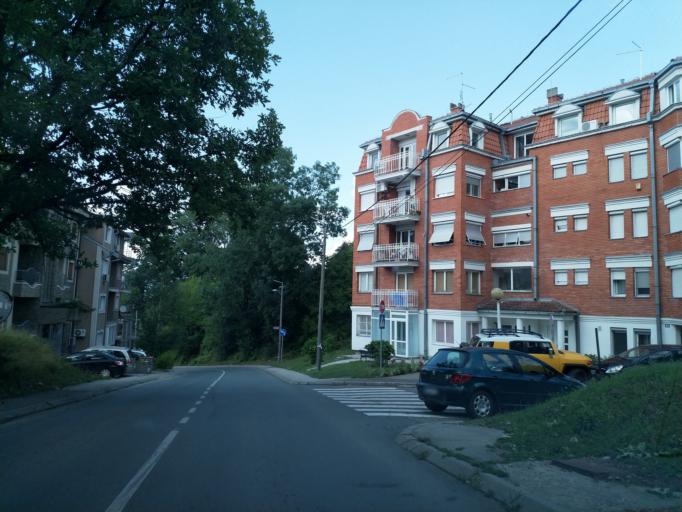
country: RS
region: Central Serbia
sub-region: Raski Okrug
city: Vrnjacka Banja
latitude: 43.6226
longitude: 20.8975
